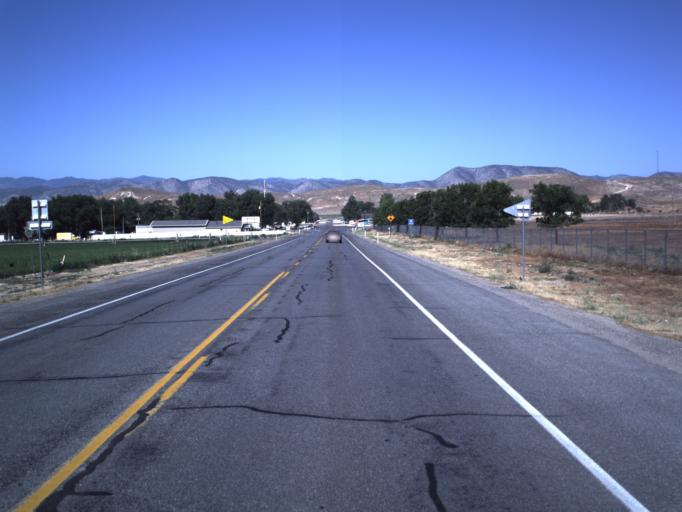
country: US
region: Utah
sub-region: Sanpete County
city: Gunnison
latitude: 39.1600
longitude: -111.8129
